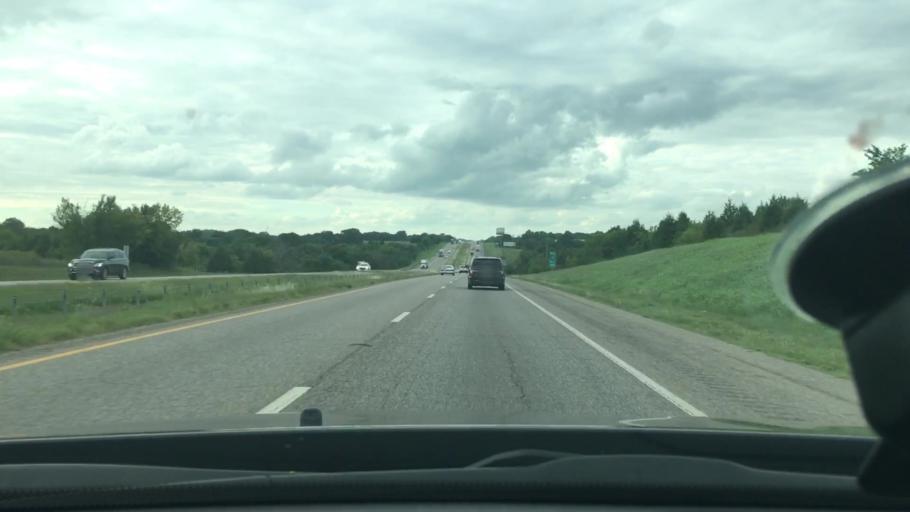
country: US
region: Oklahoma
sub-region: Cleveland County
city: Noble
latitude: 35.1000
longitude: -97.4274
